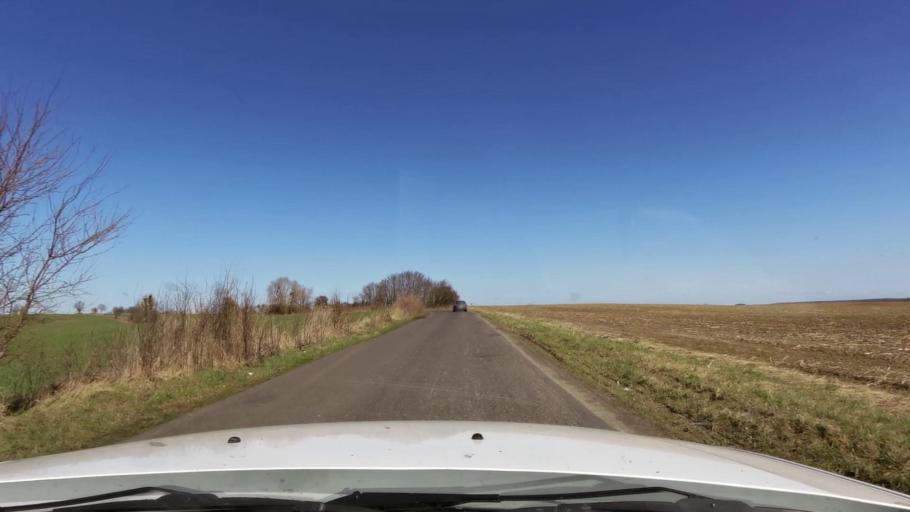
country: PL
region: West Pomeranian Voivodeship
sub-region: Powiat gryfinski
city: Cedynia
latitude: 52.8669
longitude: 14.2901
